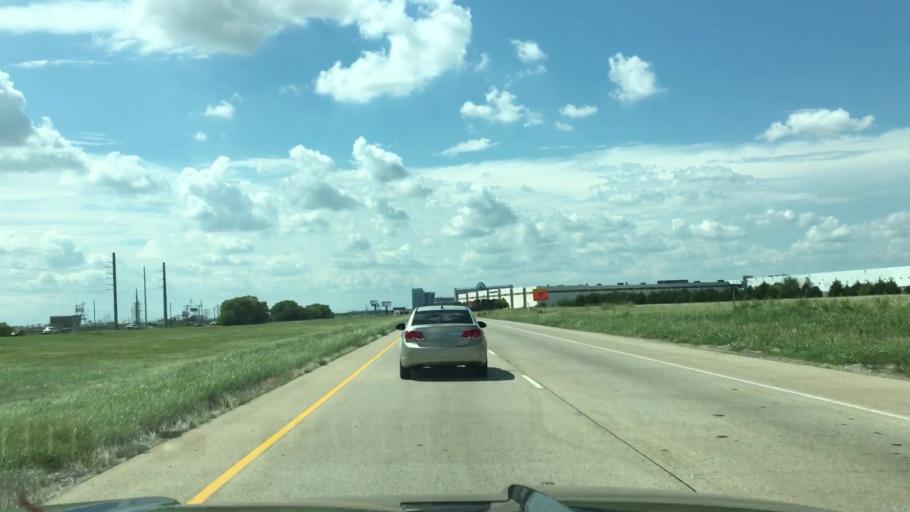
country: US
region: Texas
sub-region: Denton County
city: Roanoke
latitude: 33.0255
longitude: -97.2615
